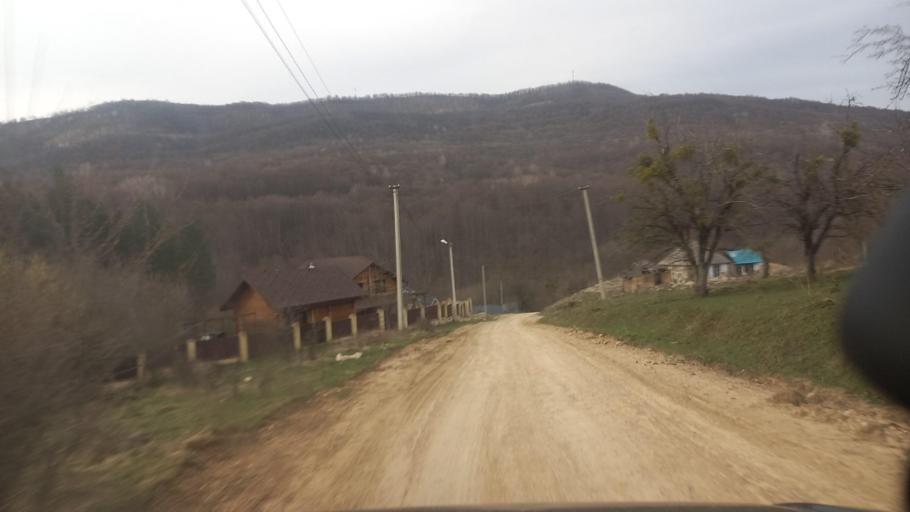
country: RU
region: Adygeya
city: Kamennomostskiy
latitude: 44.2045
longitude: 40.0012
